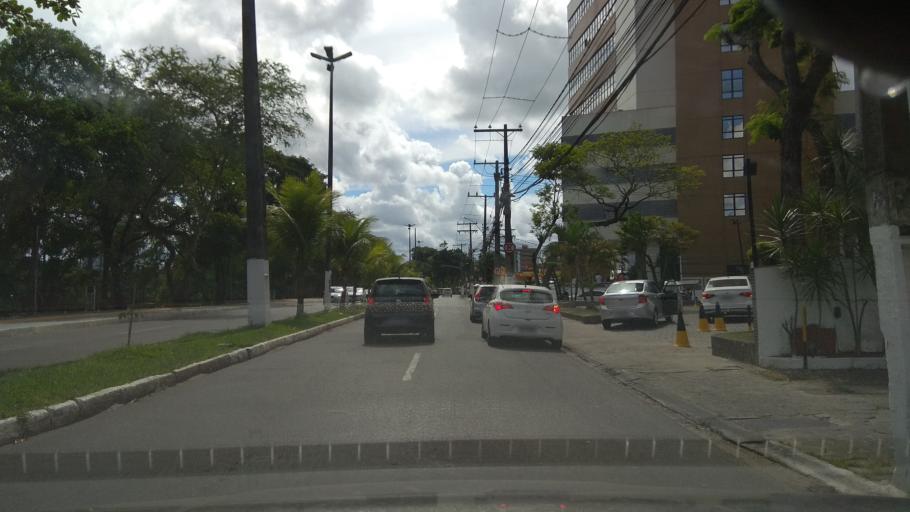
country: BR
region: Bahia
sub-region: Itabuna
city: Itabuna
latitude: -14.7979
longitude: -39.2751
